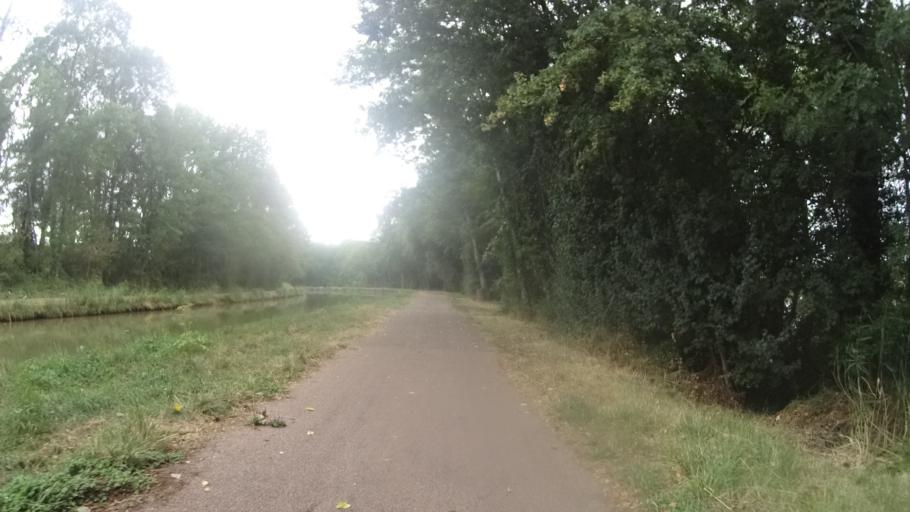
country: FR
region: Bourgogne
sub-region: Departement de la Nievre
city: Sermoise-sur-Loire
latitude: 46.9635
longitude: 3.1903
